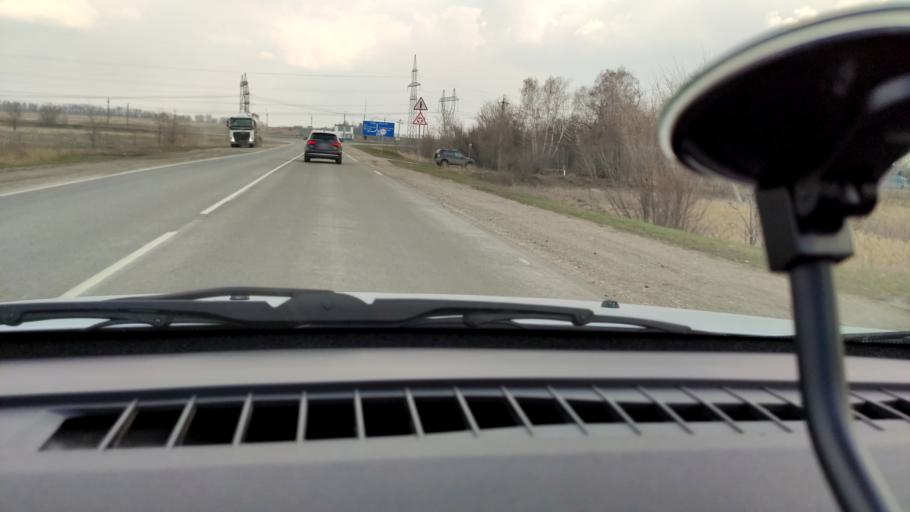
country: RU
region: Samara
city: Dubovyy Umet
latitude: 53.0637
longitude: 50.3738
